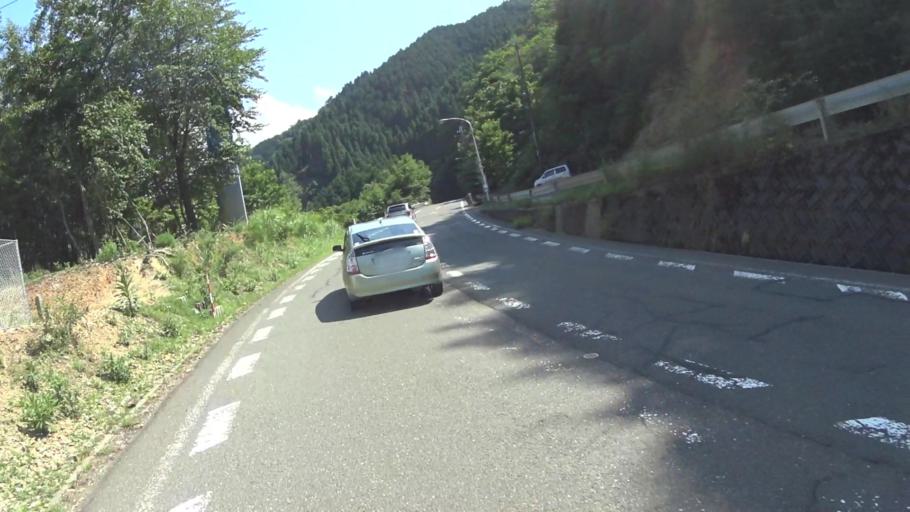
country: JP
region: Fukui
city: Obama
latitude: 35.3890
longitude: 135.5869
